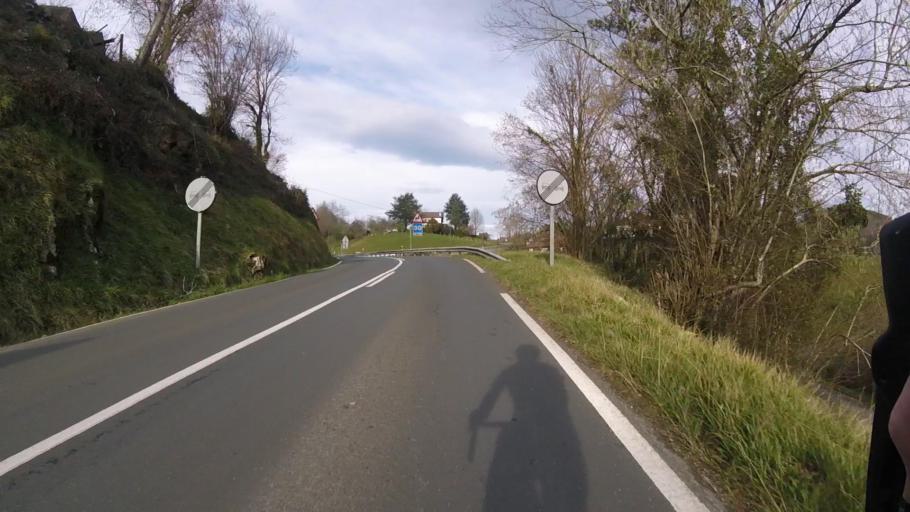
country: ES
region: Basque Country
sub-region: Provincia de Guipuzcoa
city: Lezo
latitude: 43.2996
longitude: -1.8546
